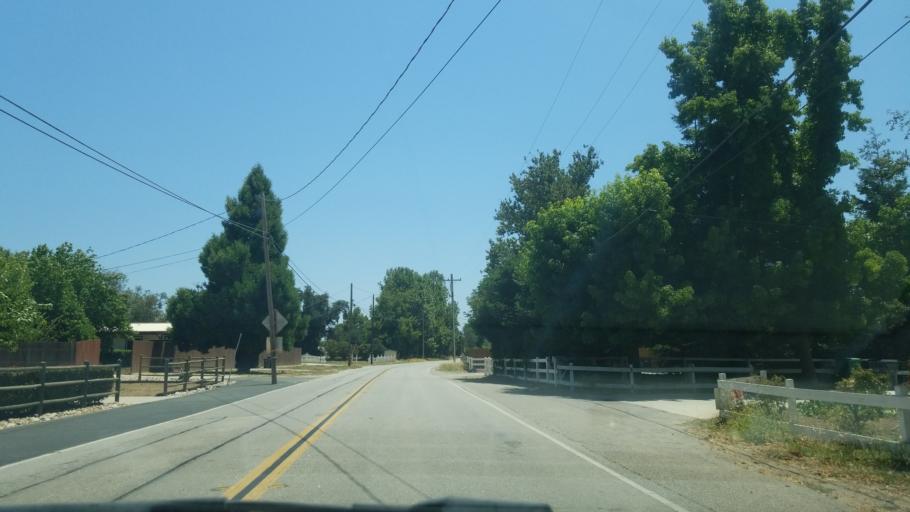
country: US
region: California
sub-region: San Luis Obispo County
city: Atascadero
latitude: 35.4955
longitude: -120.6487
